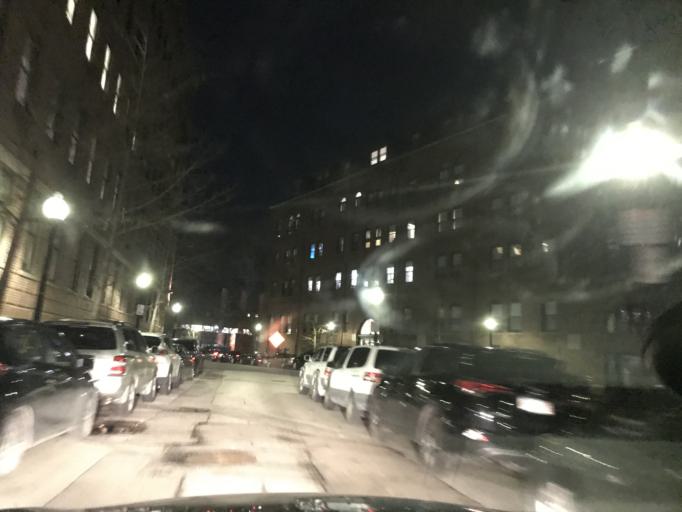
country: US
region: Massachusetts
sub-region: Suffolk County
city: Boston
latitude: 42.3407
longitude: -71.0676
